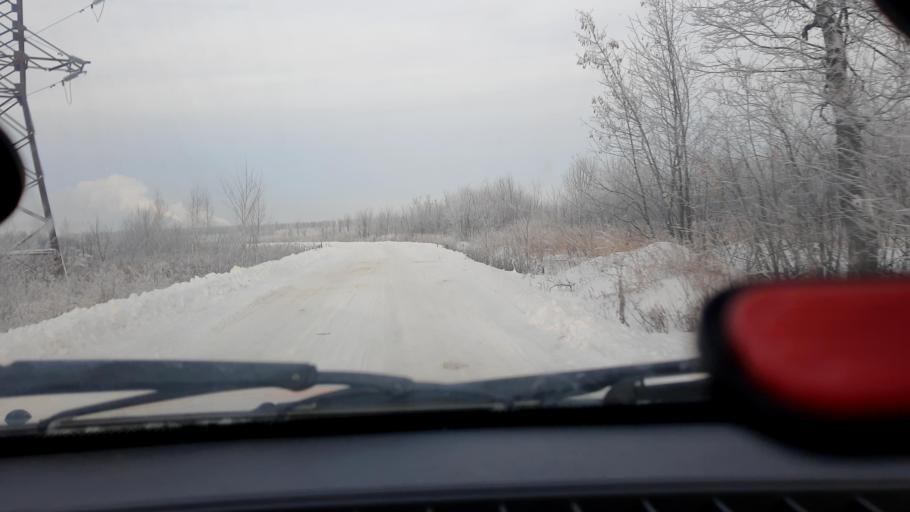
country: RU
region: Bashkortostan
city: Iglino
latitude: 54.7322
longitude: 56.2381
